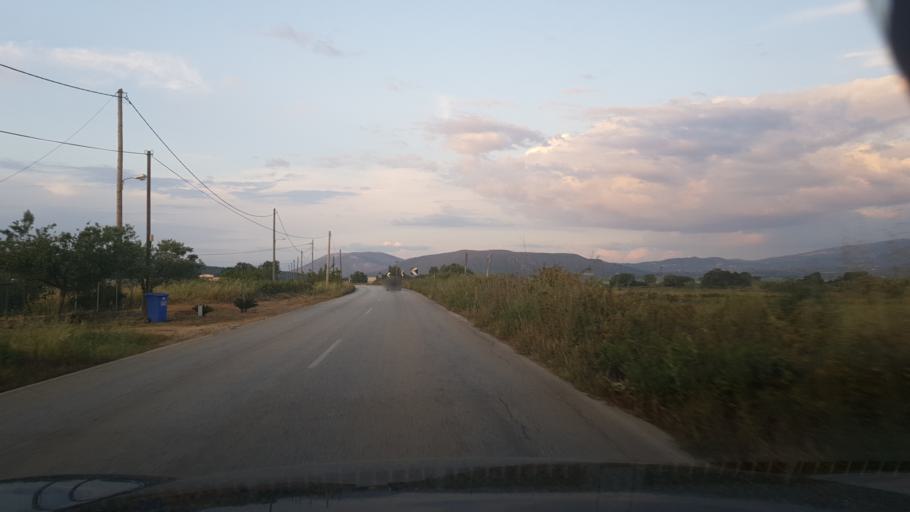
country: GR
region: West Greece
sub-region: Nomos Aitolias kai Akarnanias
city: Vonitsa
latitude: 38.8724
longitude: 20.8121
